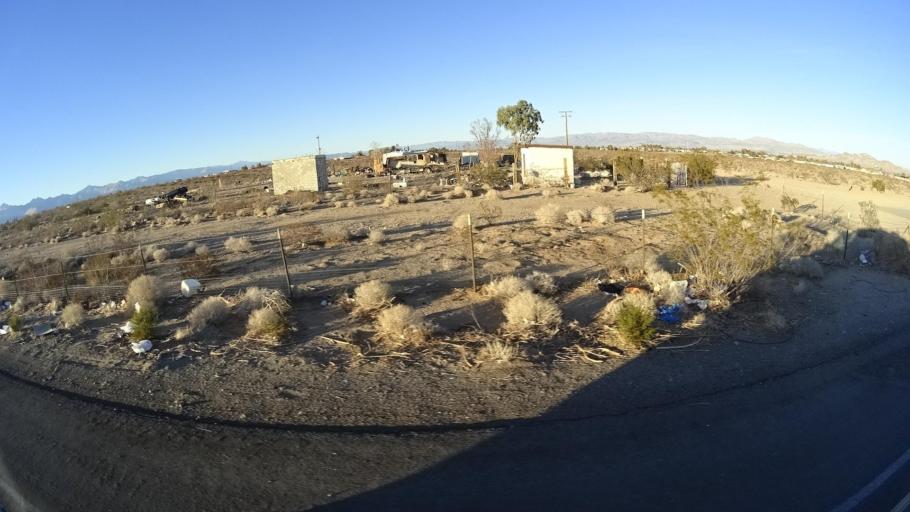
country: US
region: California
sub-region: Kern County
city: Ridgecrest
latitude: 35.6080
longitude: -117.7059
